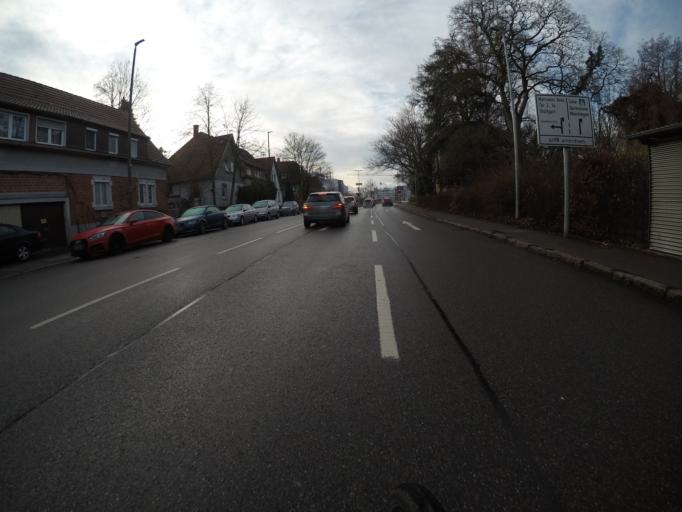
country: DE
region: Baden-Wuerttemberg
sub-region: Regierungsbezirk Stuttgart
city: Sindelfingen
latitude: 48.7080
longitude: 8.9939
